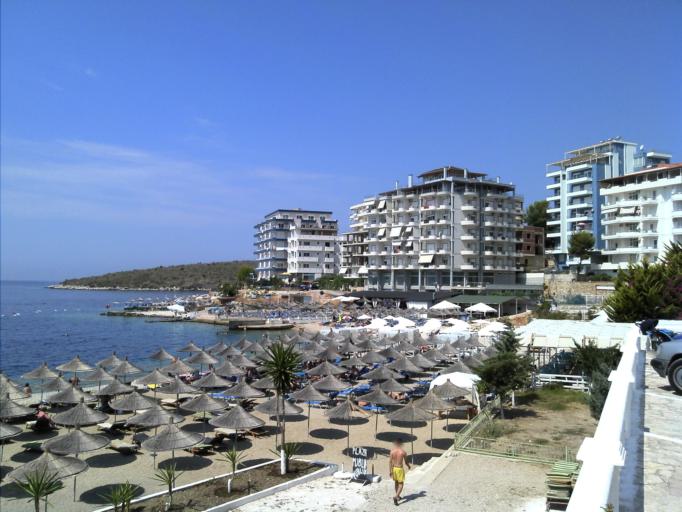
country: AL
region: Vlore
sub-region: Rrethi i Sarandes
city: Sarande
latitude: 39.8709
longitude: 19.9949
